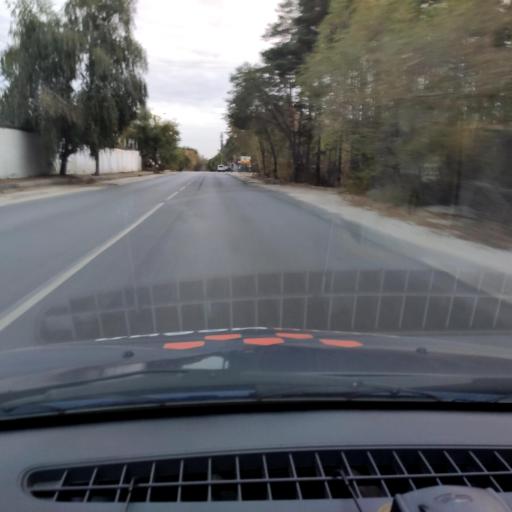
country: RU
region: Voronezj
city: Pridonskoy
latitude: 51.6815
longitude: 39.0956
